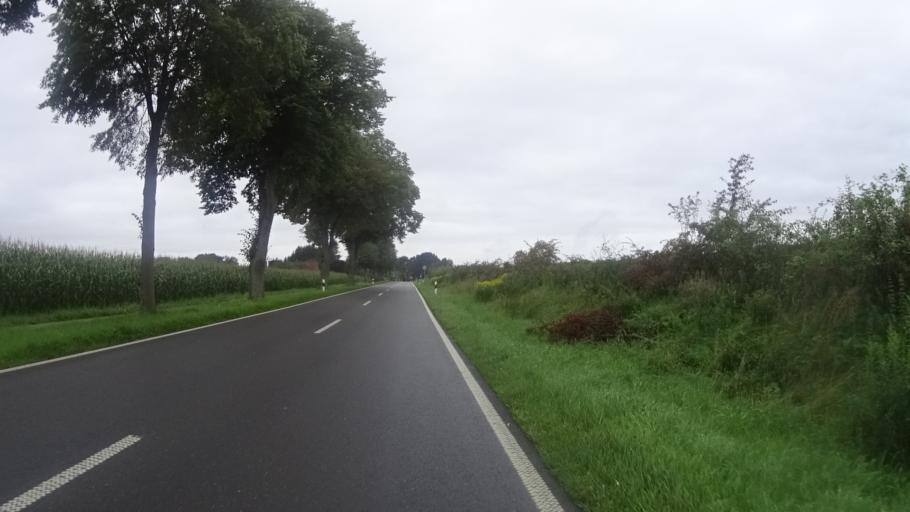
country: DE
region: Schleswig-Holstein
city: Roseburg
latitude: 53.5315
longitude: 10.6514
